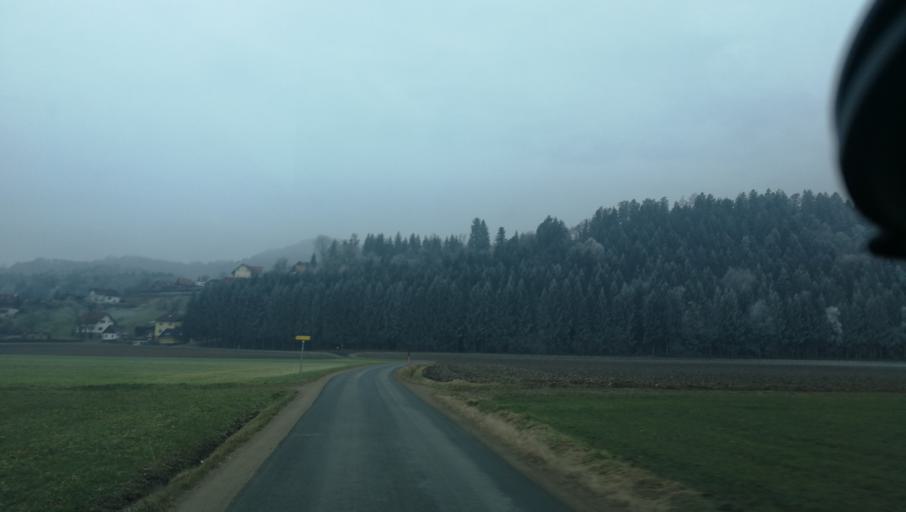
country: AT
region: Styria
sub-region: Politischer Bezirk Deutschlandsberg
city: Stainz
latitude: 46.8994
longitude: 15.2430
